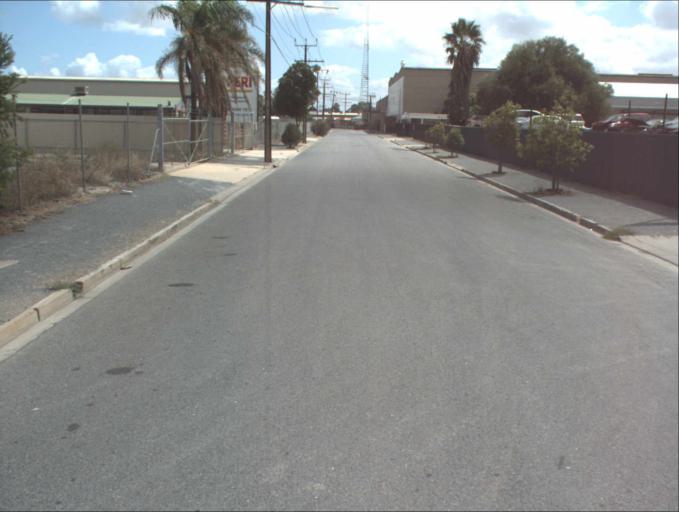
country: AU
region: South Australia
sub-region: Port Adelaide Enfield
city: Blair Athol
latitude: -34.8468
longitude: 138.5888
